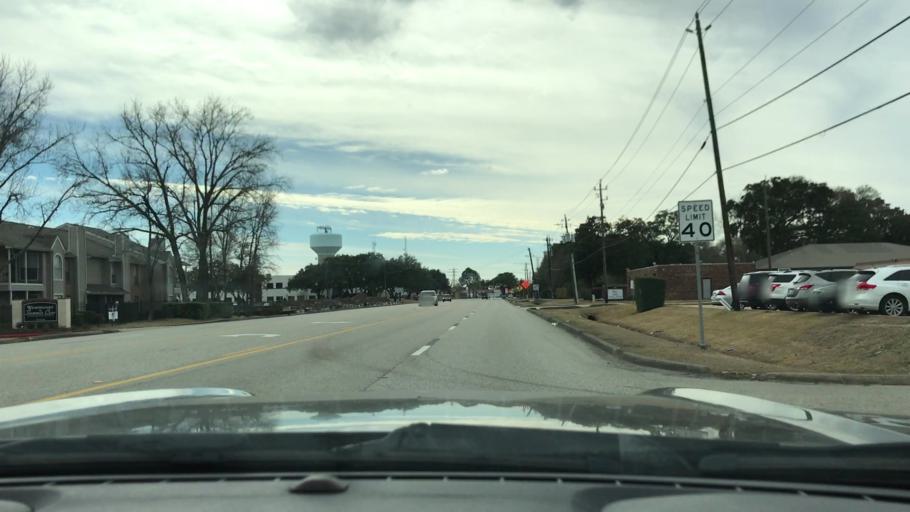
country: US
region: Texas
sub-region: Galveston County
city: Friendswood
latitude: 29.5940
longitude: -95.1798
